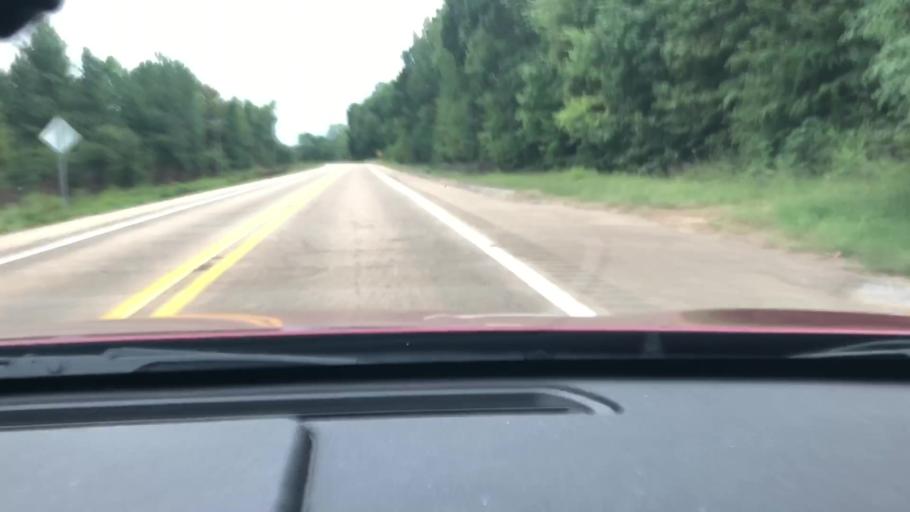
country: US
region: Arkansas
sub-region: Miller County
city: Texarkana
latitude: 33.4167
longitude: -93.8125
